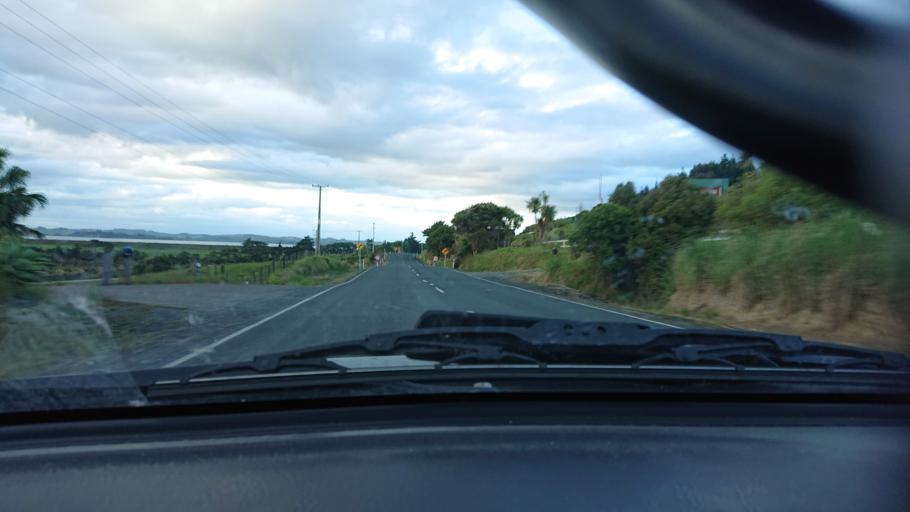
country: NZ
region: Auckland
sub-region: Auckland
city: Wellsford
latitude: -36.4471
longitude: 174.4334
